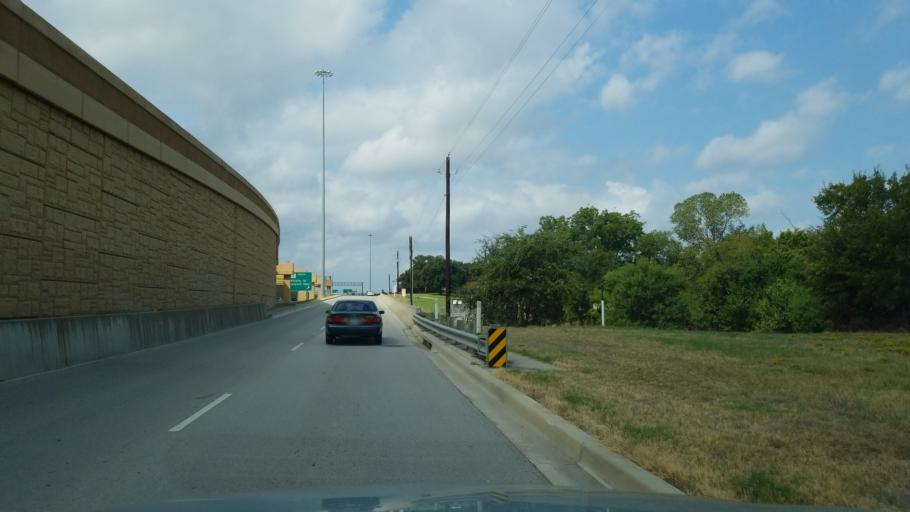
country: US
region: Texas
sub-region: Tarrant County
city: Euless
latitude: 32.8384
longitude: -97.1106
